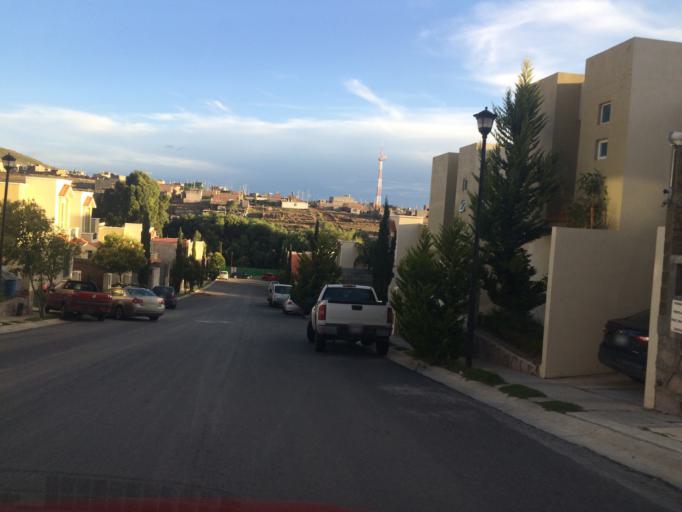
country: MX
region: Zacatecas
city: Zacatecas
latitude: 22.7477
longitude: -102.5845
